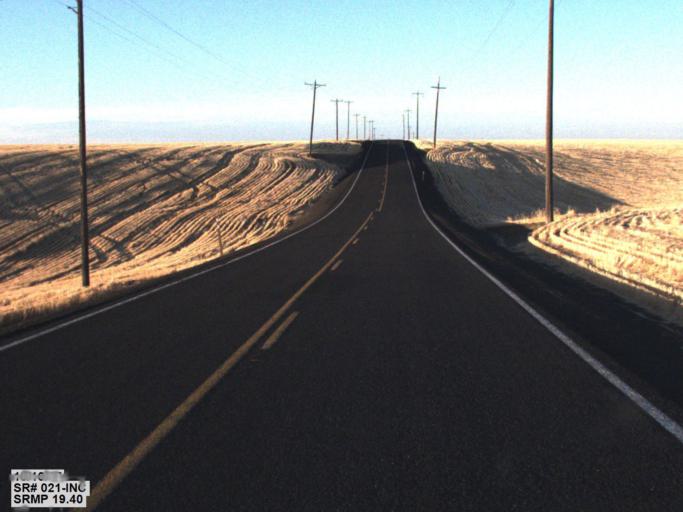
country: US
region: Washington
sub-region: Adams County
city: Ritzville
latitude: 46.9011
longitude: -118.5679
